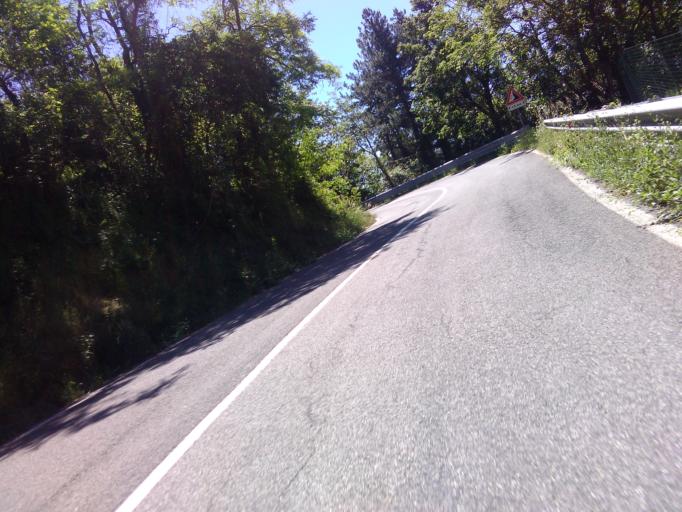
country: IT
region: Tuscany
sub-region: Provincia di Massa-Carrara
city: Pontremoli
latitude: 44.4497
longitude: 9.9078
